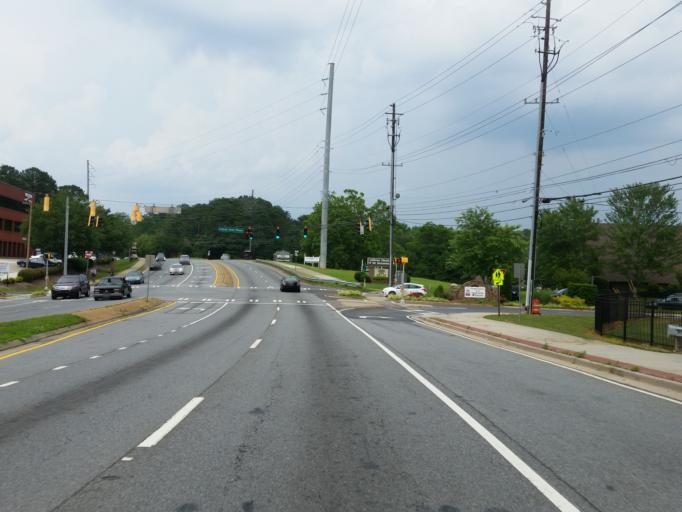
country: US
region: Georgia
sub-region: Fulton County
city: Sandy Springs
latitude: 33.9779
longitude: -84.4378
